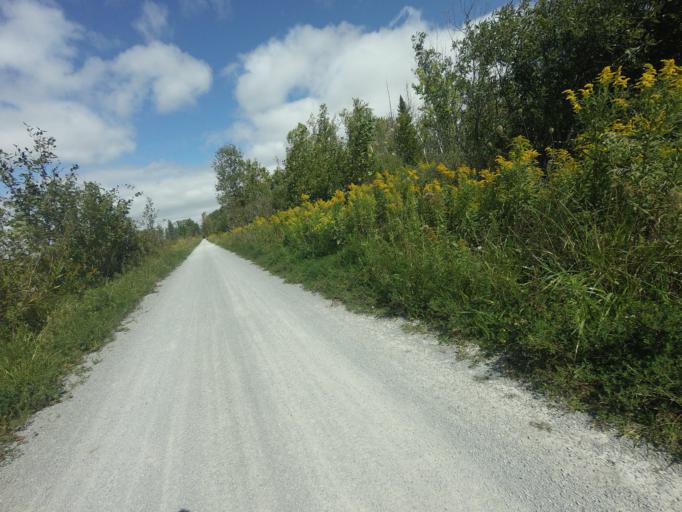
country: CA
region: Ontario
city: Uxbridge
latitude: 44.1448
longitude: -79.0866
